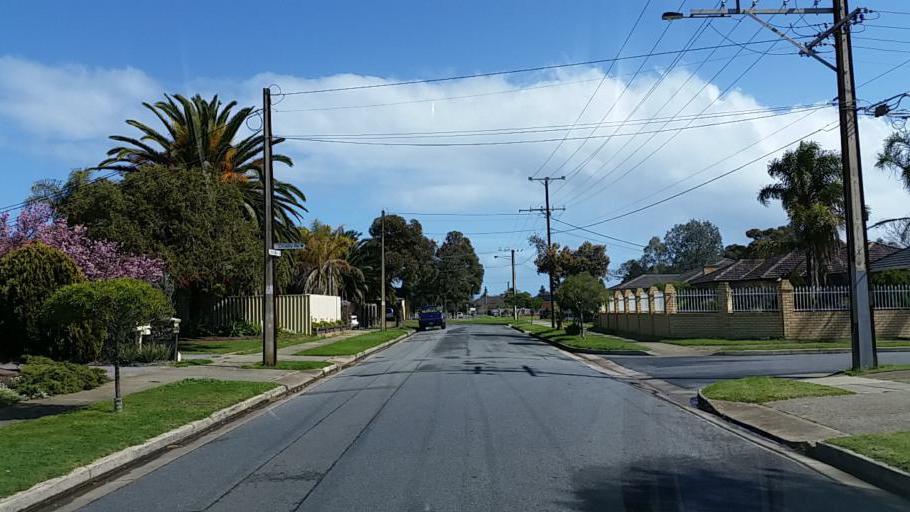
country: AU
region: South Australia
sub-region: Charles Sturt
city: Seaton
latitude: -34.9033
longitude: 138.5097
